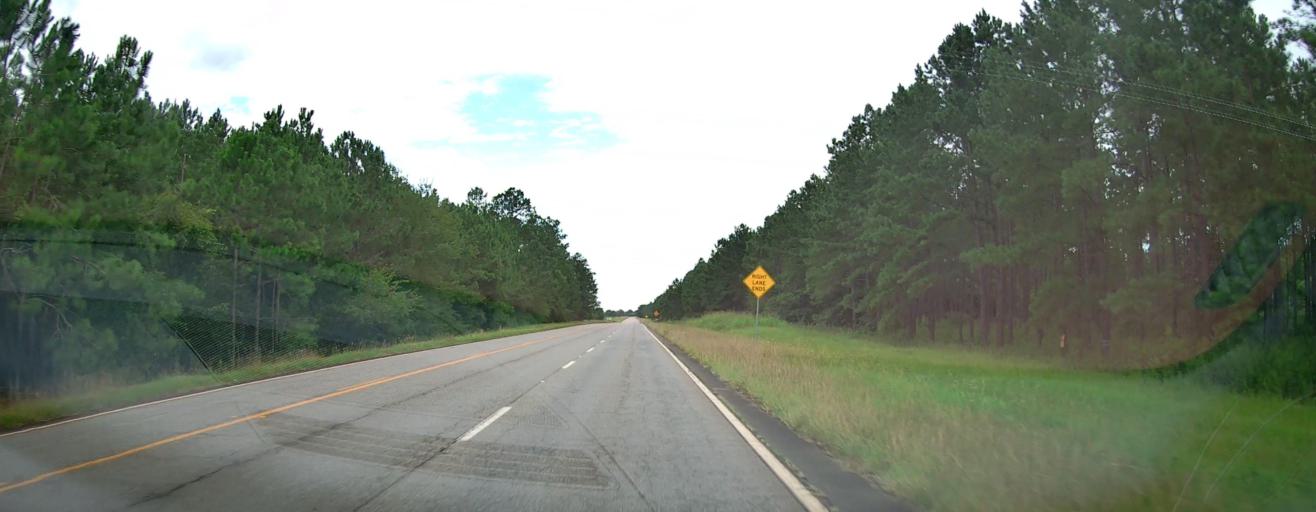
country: US
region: Georgia
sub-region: Marion County
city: Buena Vista
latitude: 32.2910
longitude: -84.4531
